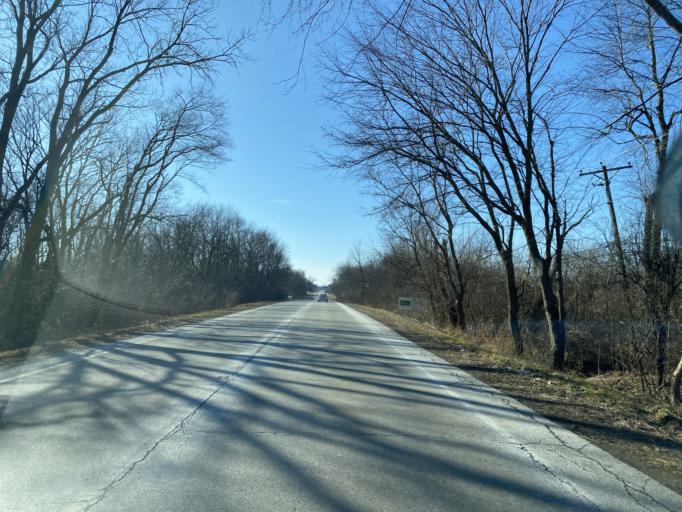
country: US
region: Illinois
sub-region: Will County
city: Lockport
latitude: 41.6168
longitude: -88.0349
